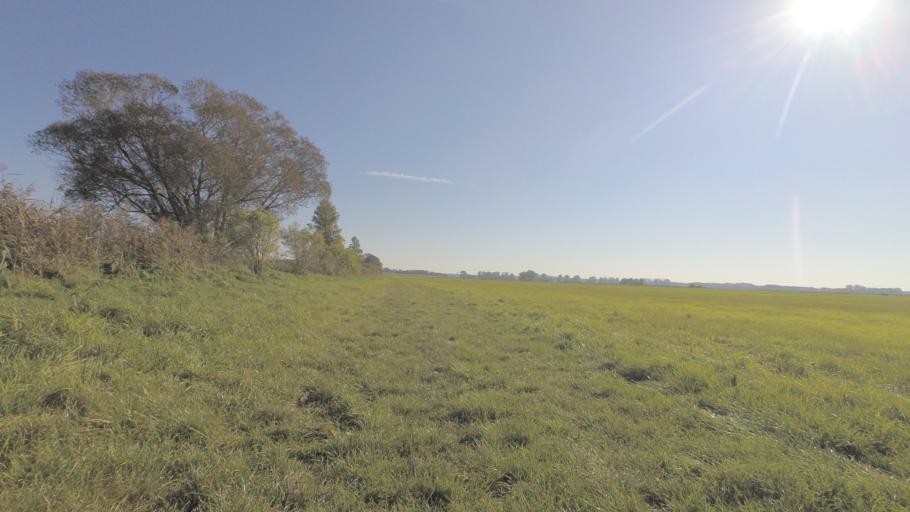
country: DE
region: Brandenburg
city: Rangsdorf
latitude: 52.3036
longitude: 13.3581
